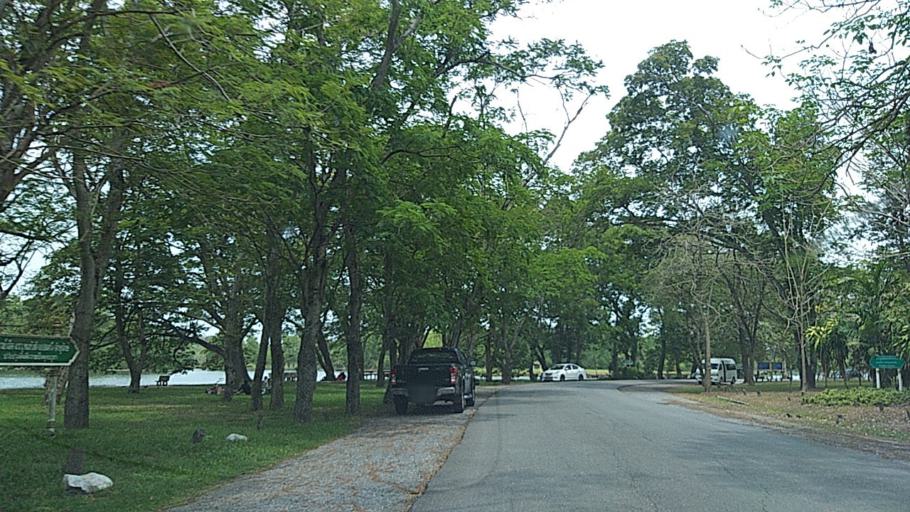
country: TH
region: Bangkok
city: Thawi Watthana
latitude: 13.7718
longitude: 100.3151
